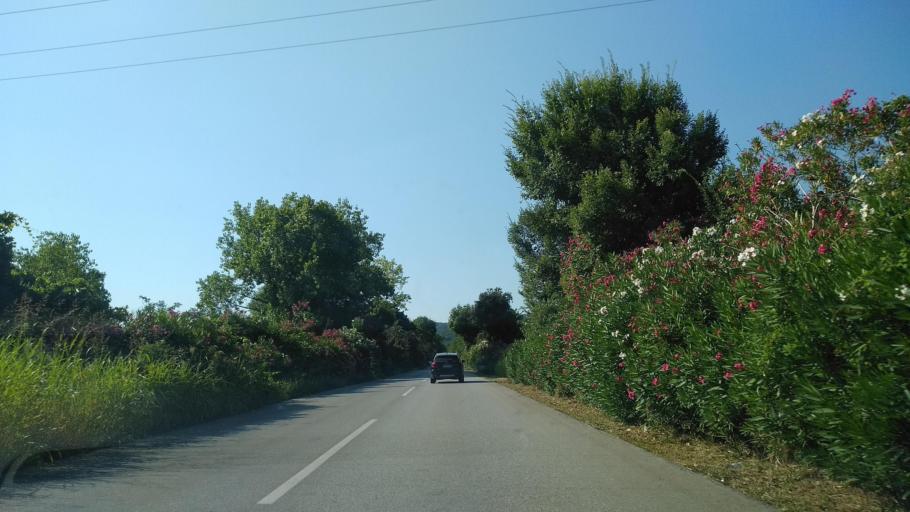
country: GR
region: Central Macedonia
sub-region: Nomos Chalkidikis
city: Stratonion
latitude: 40.4615
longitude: 23.8157
